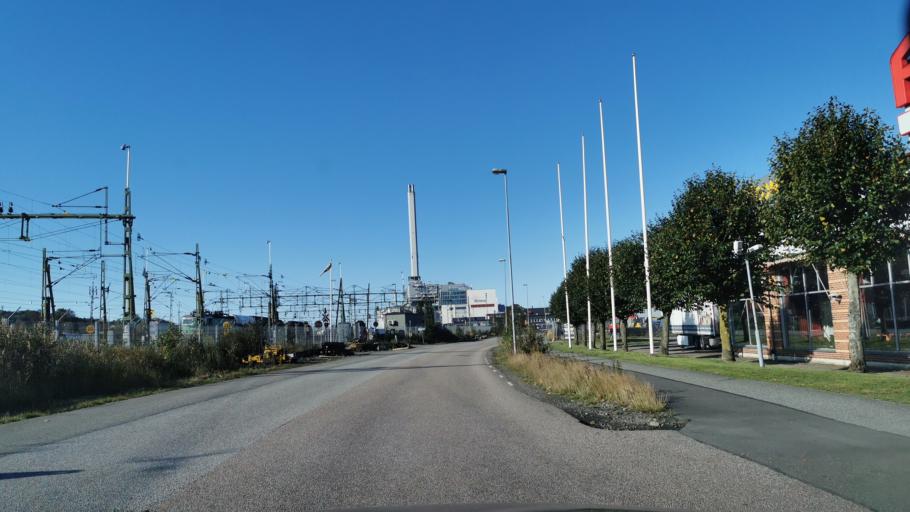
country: SE
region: Vaestra Goetaland
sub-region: Partille Kommun
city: Partille
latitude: 57.7326
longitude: 12.0629
